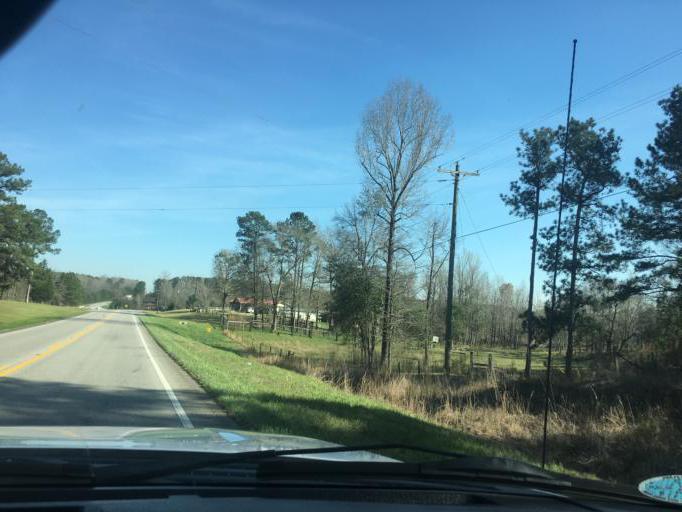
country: US
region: Alabama
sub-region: Lee County
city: Auburn
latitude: 32.4341
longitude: -85.4730
